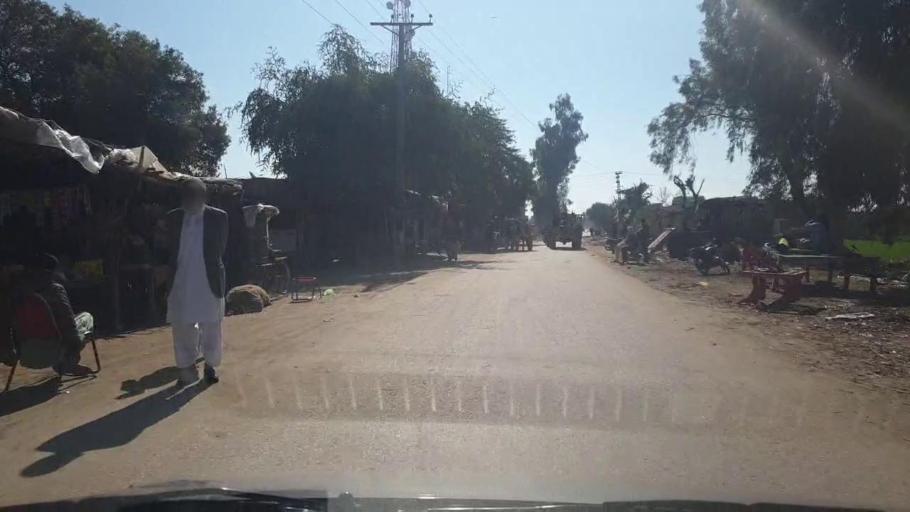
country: PK
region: Sindh
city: Bozdar
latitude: 27.1818
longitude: 68.6391
